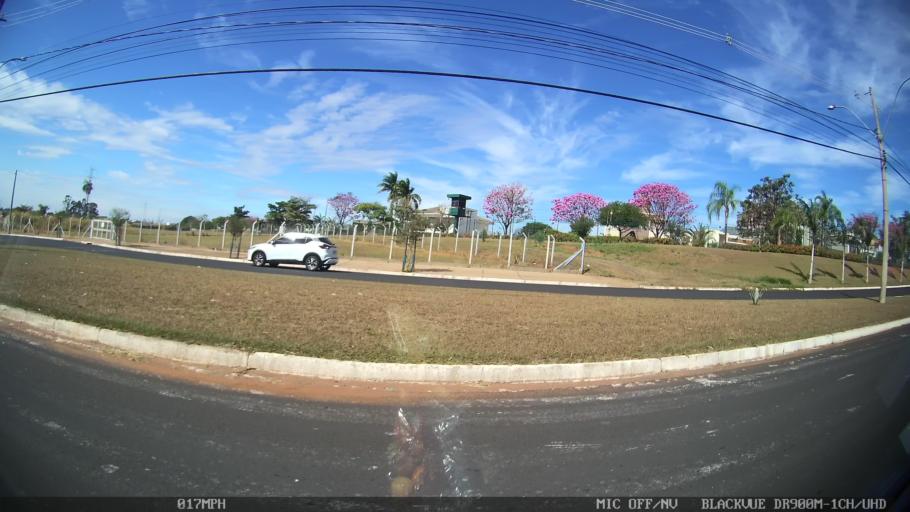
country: BR
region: Sao Paulo
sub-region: Sao Jose Do Rio Preto
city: Sao Jose do Rio Preto
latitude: -20.8193
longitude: -49.4805
